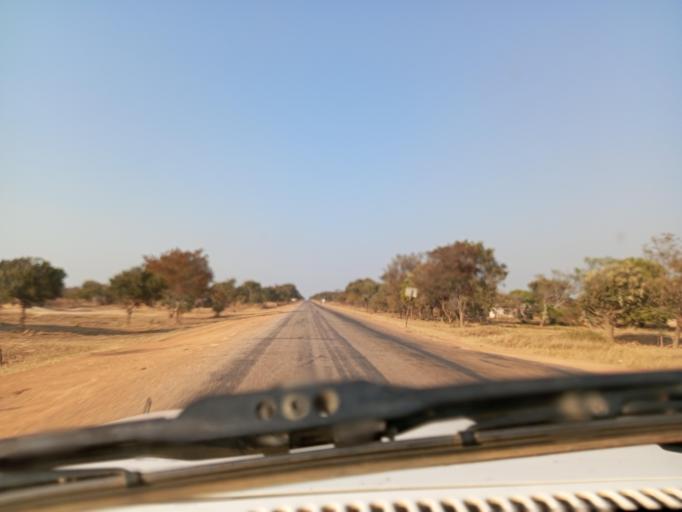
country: ZM
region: Northern
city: Mpika
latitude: -12.3768
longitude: 31.0997
